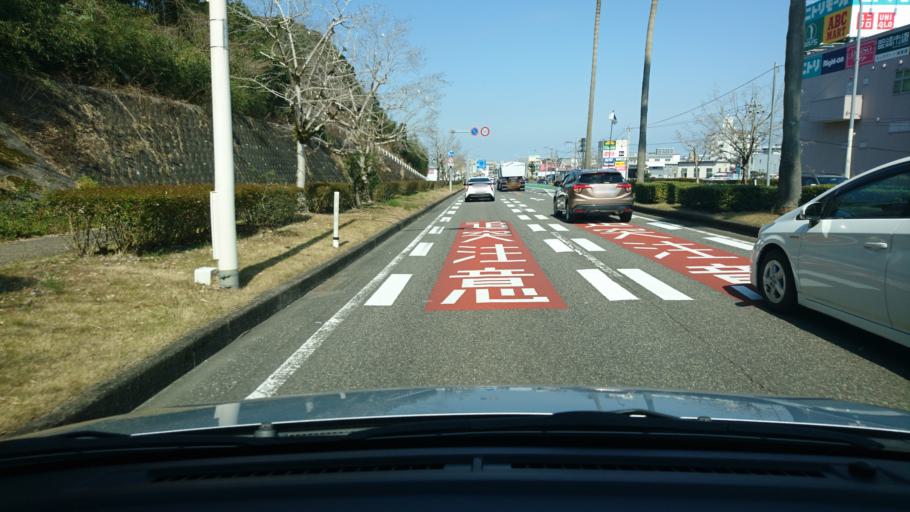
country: JP
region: Miyazaki
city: Miyazaki-shi
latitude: 31.8848
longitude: 131.4115
